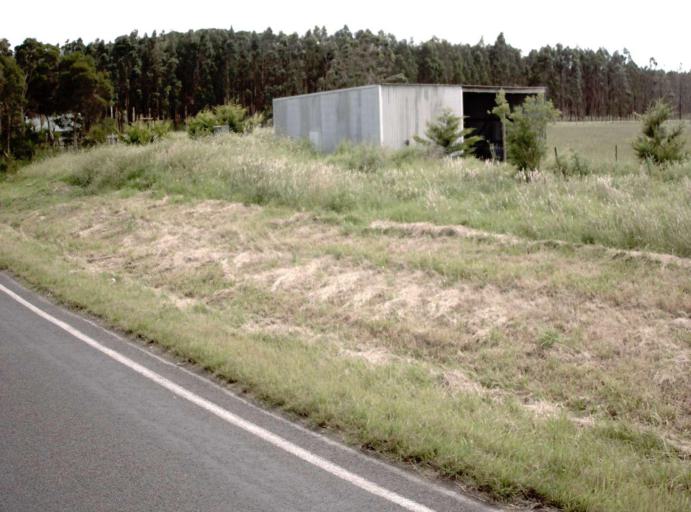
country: AU
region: Victoria
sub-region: Latrobe
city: Morwell
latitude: -38.1631
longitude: 146.4070
